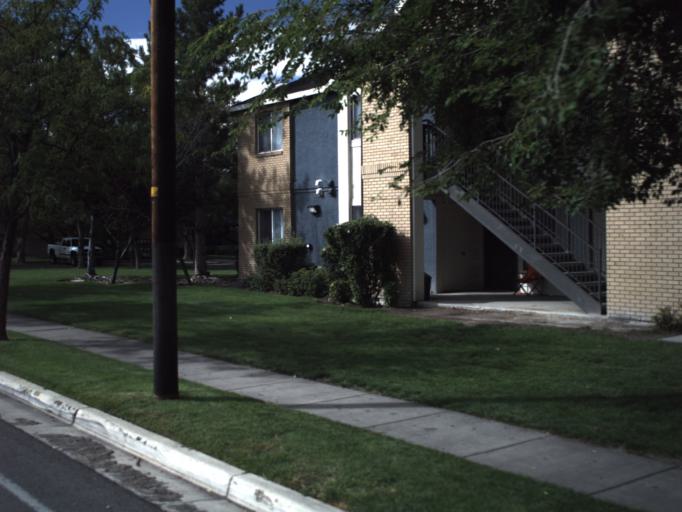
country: US
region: Utah
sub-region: Salt Lake County
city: Salt Lake City
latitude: 40.7969
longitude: -111.9393
